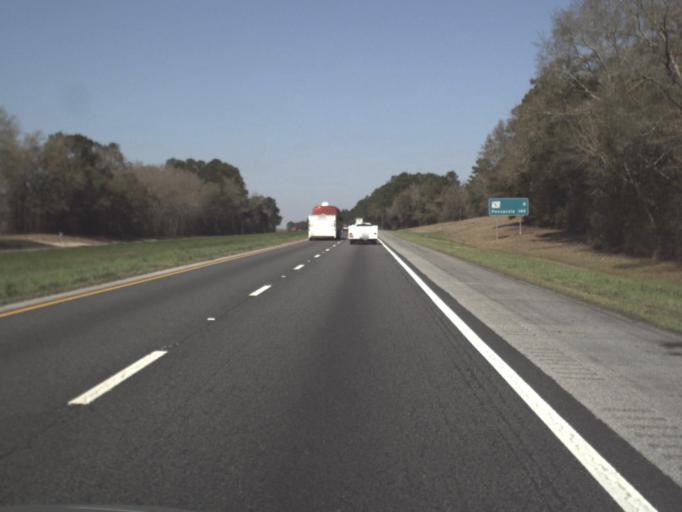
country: US
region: Florida
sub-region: Jackson County
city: Sneads
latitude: 30.6665
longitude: -85.0549
